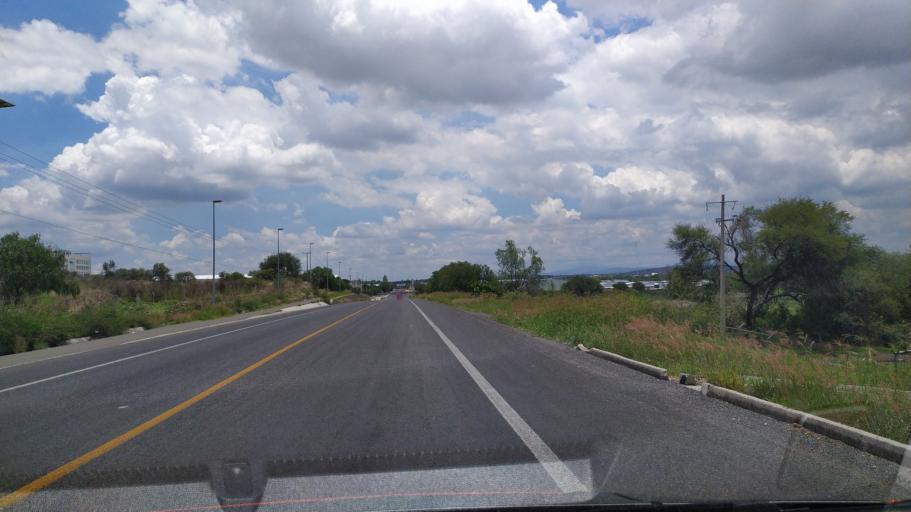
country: MX
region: Guanajuato
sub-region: Purisima del Rincon
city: Monte Grande
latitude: 21.0035
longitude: -101.8921
